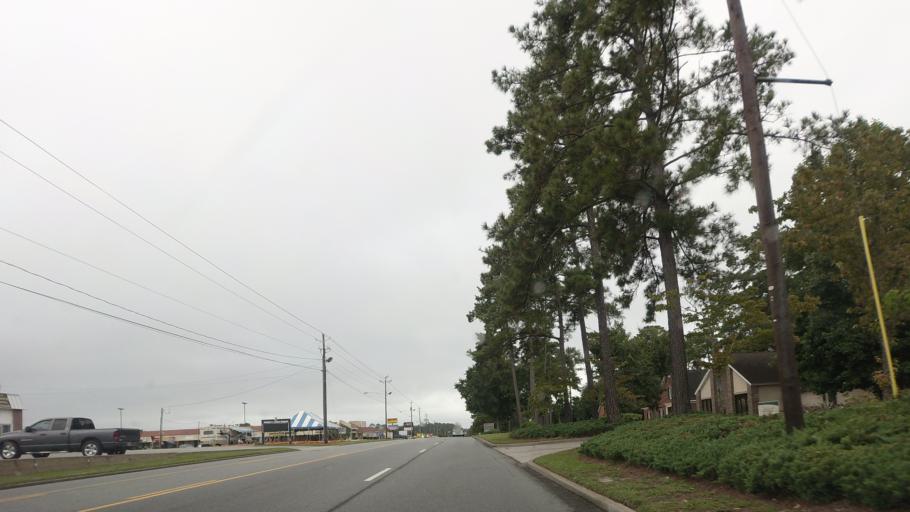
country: US
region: Georgia
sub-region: Lowndes County
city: Remerton
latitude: 30.8721
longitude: -83.2911
